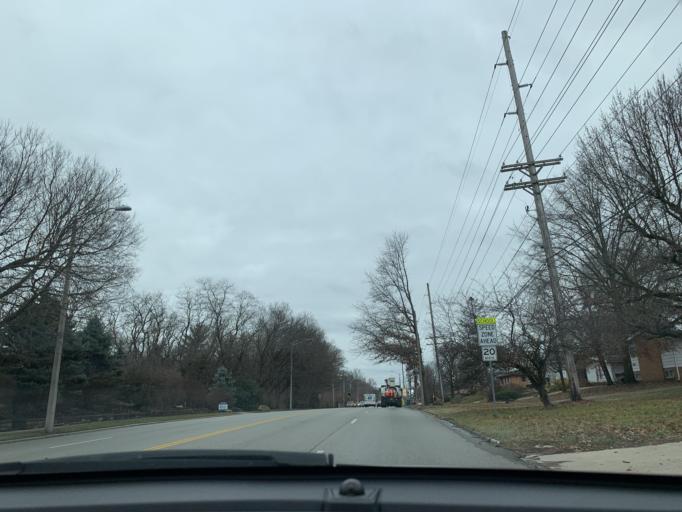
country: US
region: Illinois
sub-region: Sangamon County
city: Leland Grove
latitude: 39.7741
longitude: -89.6869
